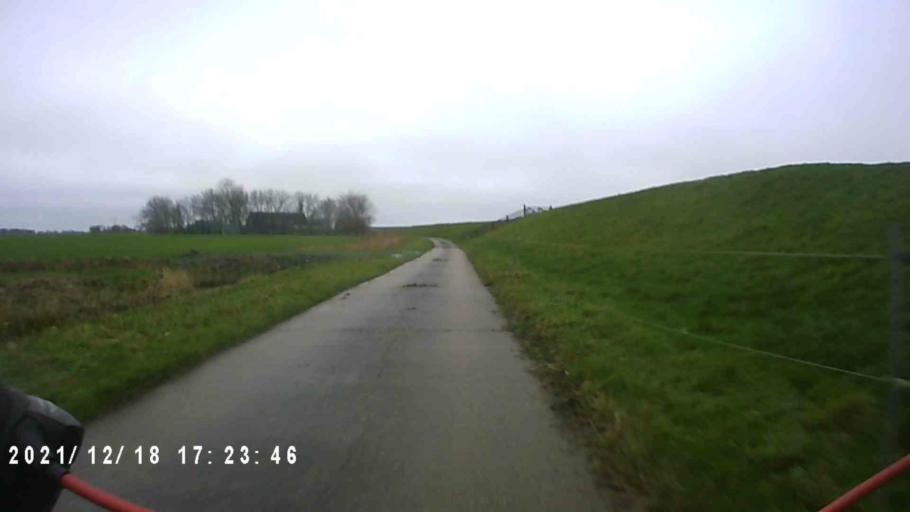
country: NL
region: Friesland
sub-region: Gemeente Dongeradeel
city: Holwerd
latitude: 53.3648
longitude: 5.8657
